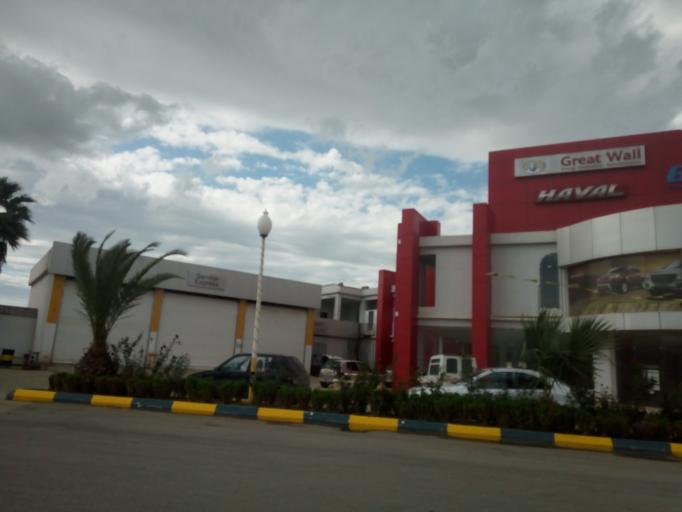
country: DZ
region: Tipaza
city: Douera
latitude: 36.6251
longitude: 2.9422
